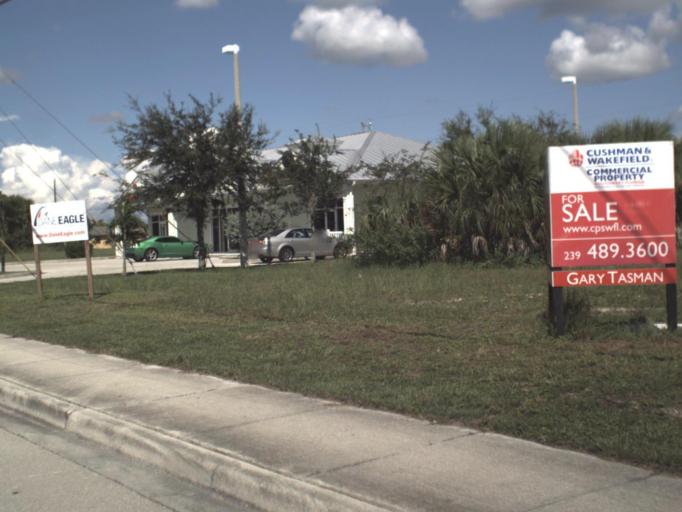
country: US
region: Florida
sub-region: Lee County
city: Lochmoor Waterway Estates
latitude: 26.6599
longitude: -81.9410
